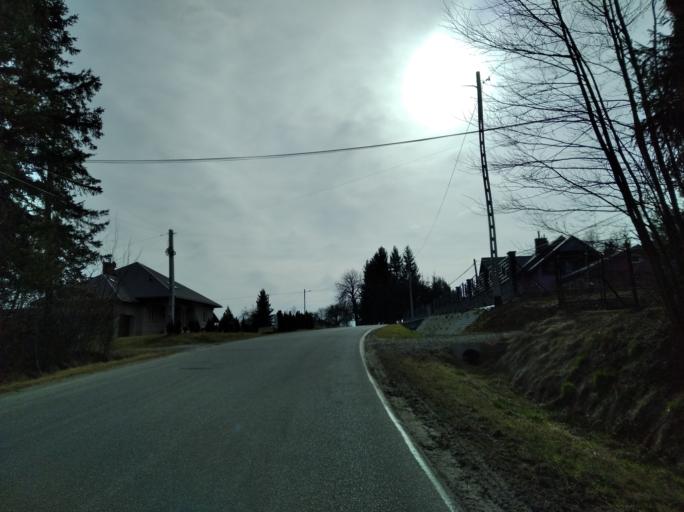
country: PL
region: Subcarpathian Voivodeship
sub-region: Powiat brzozowski
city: Orzechowka
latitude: 49.7380
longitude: 21.9416
